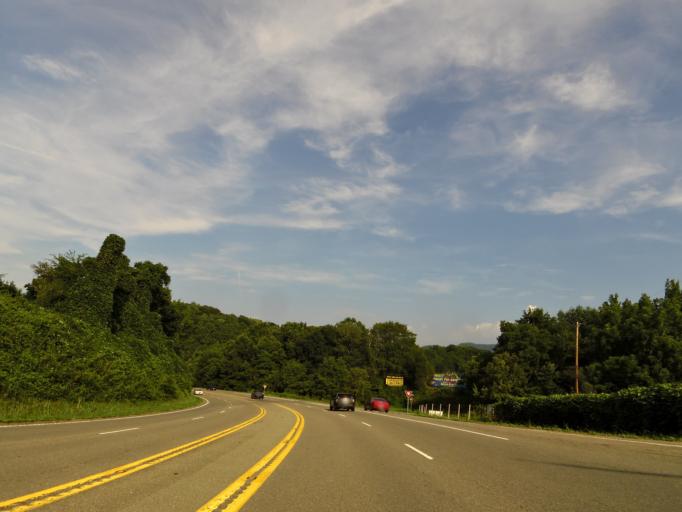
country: US
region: Tennessee
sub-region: Sevier County
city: Seymour
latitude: 35.8478
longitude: -83.7109
